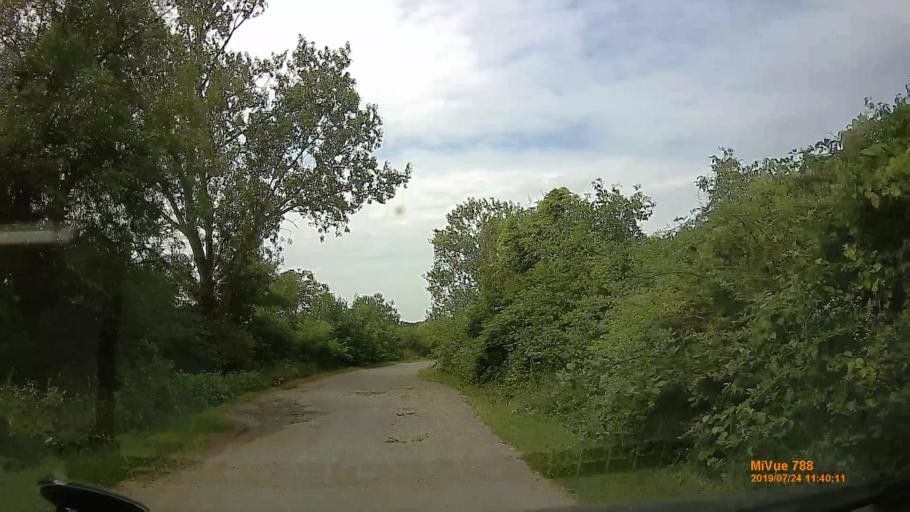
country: UA
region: Zakarpattia
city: Batiovo
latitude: 48.2368
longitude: 22.4701
